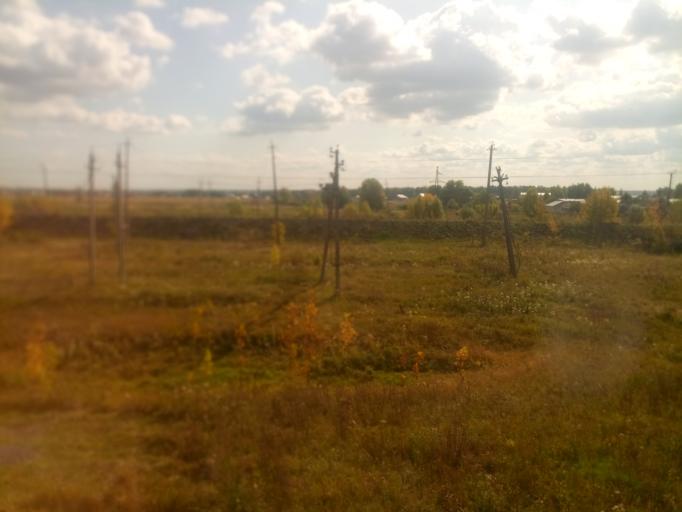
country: RU
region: Chuvashia
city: Urmary
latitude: 55.6909
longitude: 47.9564
